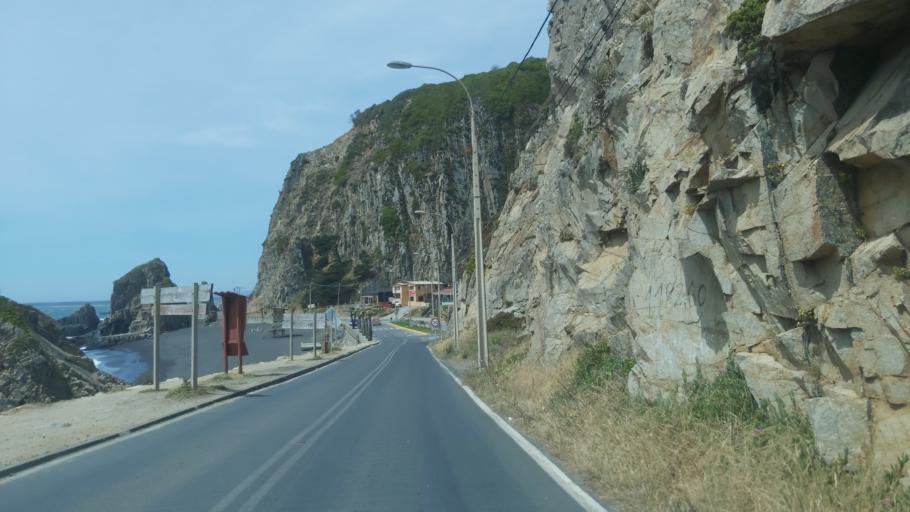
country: CL
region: Maule
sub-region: Provincia de Talca
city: Constitucion
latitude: -35.3285
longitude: -72.4313
